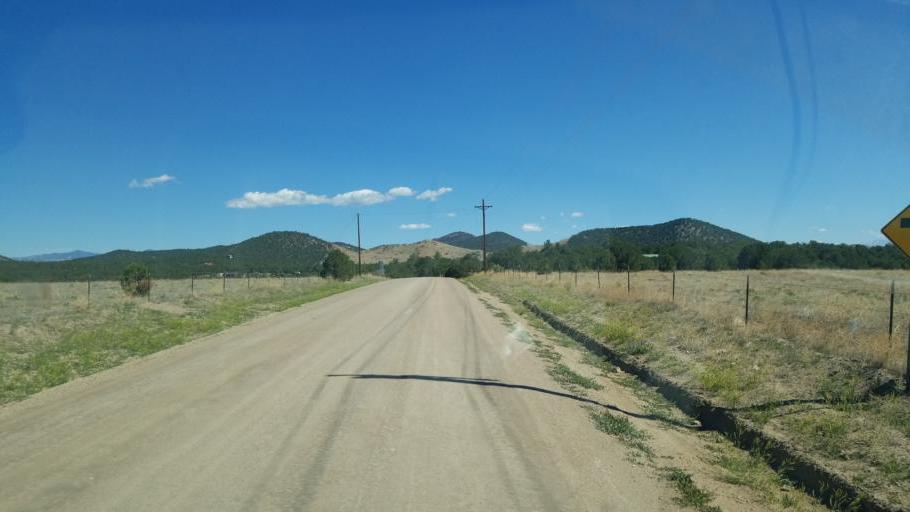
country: US
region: Colorado
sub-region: Custer County
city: Westcliffe
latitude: 38.2830
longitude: -105.5008
